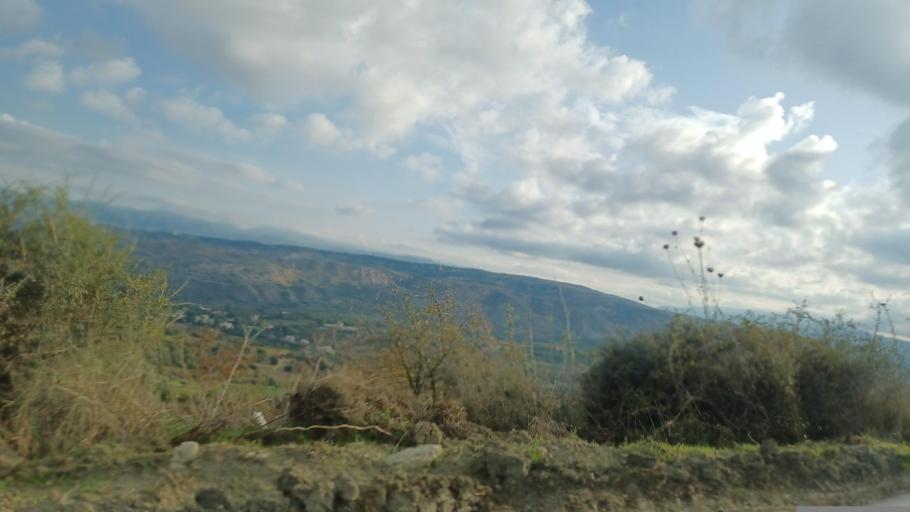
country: CY
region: Pafos
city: Tala
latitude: 34.9069
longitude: 32.4692
